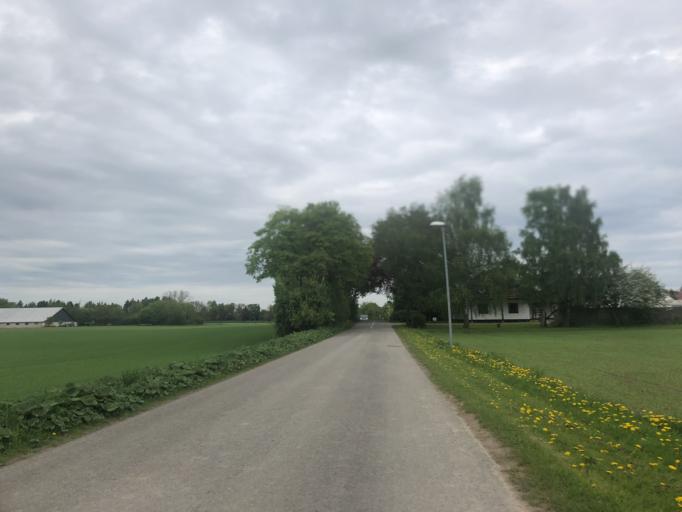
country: DK
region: Zealand
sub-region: Koge Kommune
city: Ejby
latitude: 55.4602
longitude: 12.1040
